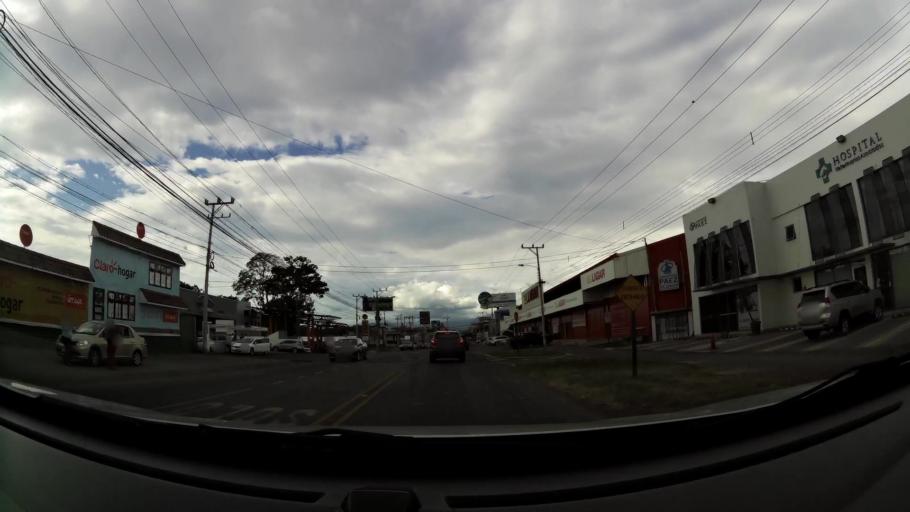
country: CR
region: San Jose
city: Santa Ana
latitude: 9.9482
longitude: -84.1924
